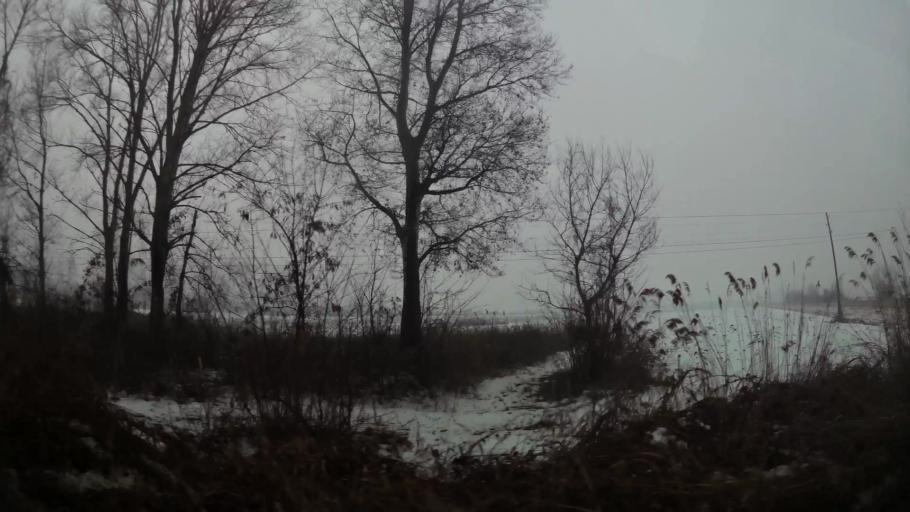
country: MK
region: Ilinden
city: Idrizovo
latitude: 41.9473
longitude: 21.5934
